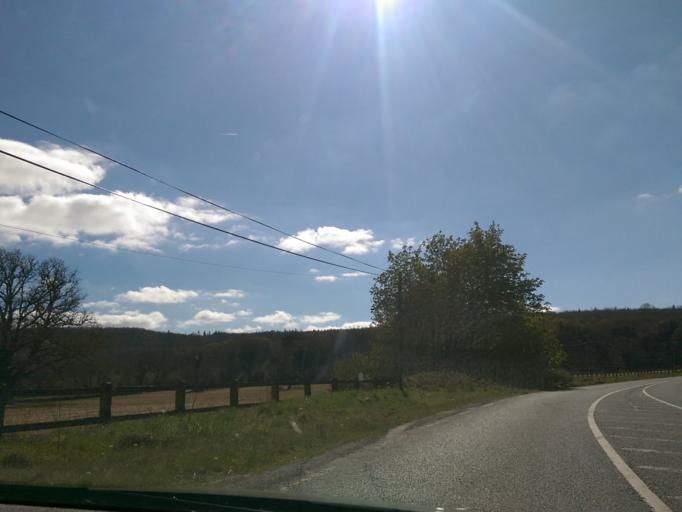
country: IE
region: Leinster
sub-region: Laois
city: Stradbally
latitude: 53.0165
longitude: -7.1168
